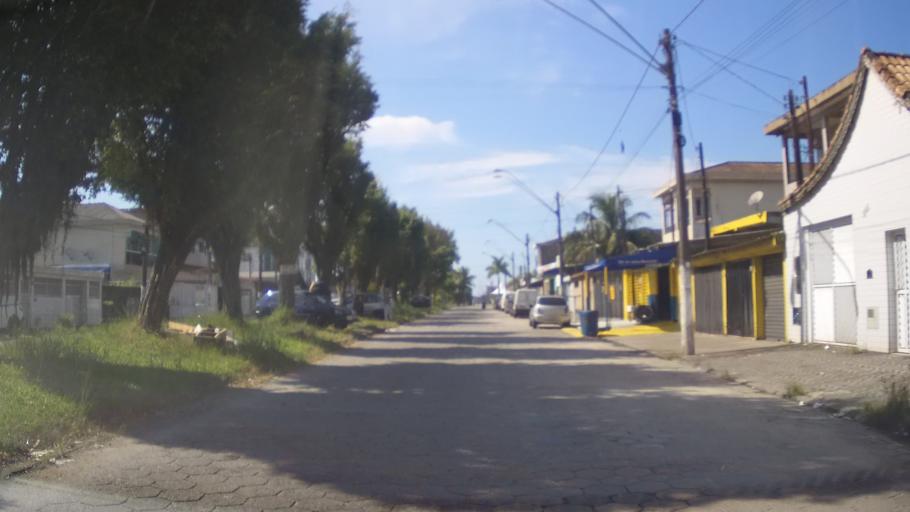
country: BR
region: Sao Paulo
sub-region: Praia Grande
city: Praia Grande
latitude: -23.9836
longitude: -46.4863
